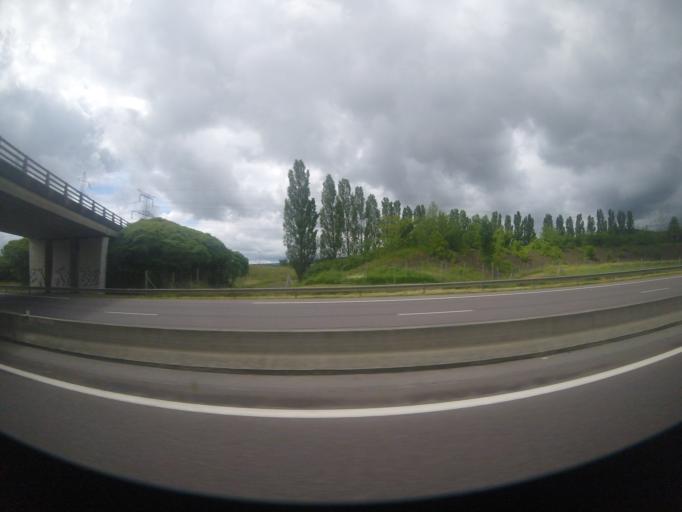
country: FR
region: Lorraine
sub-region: Departement de la Moselle
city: Maizieres-les-Metz
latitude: 49.1976
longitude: 6.1463
